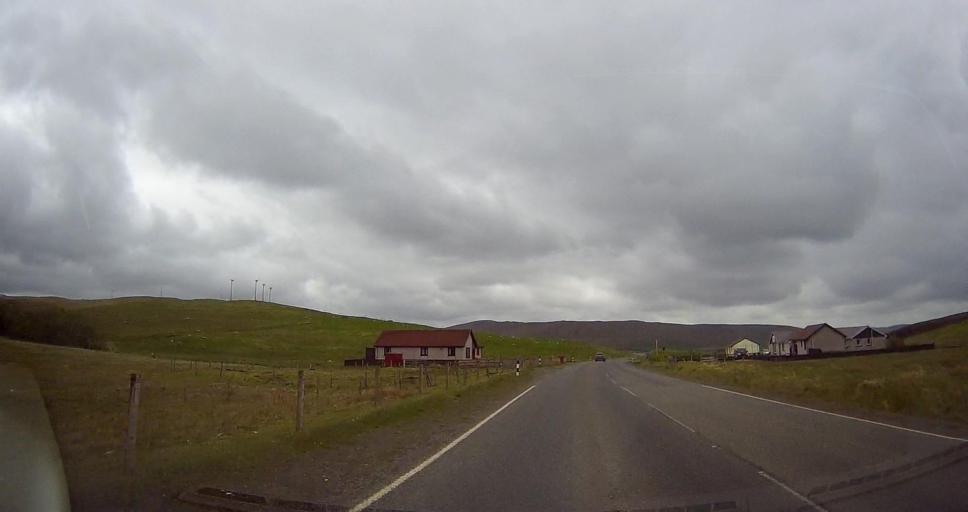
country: GB
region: Scotland
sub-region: Shetland Islands
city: Lerwick
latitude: 60.3791
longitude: -1.3414
